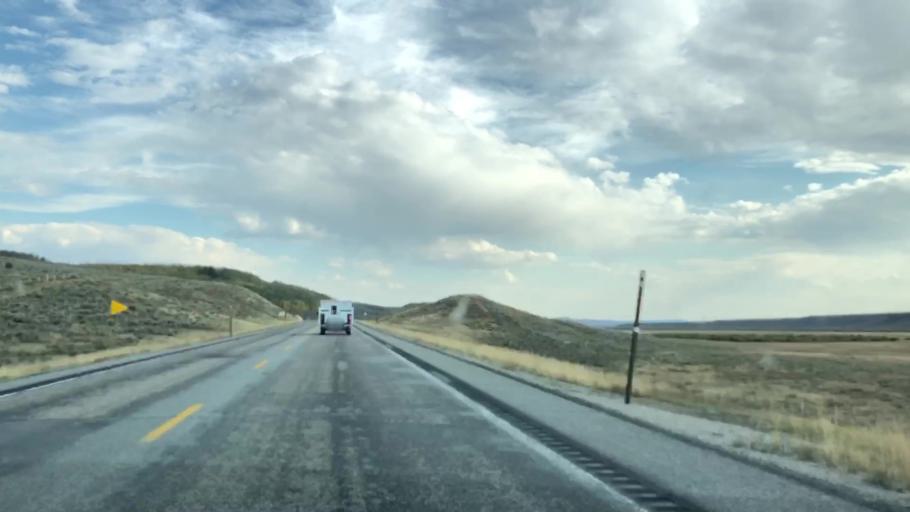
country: US
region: Wyoming
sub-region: Sublette County
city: Pinedale
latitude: 43.0938
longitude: -110.1662
